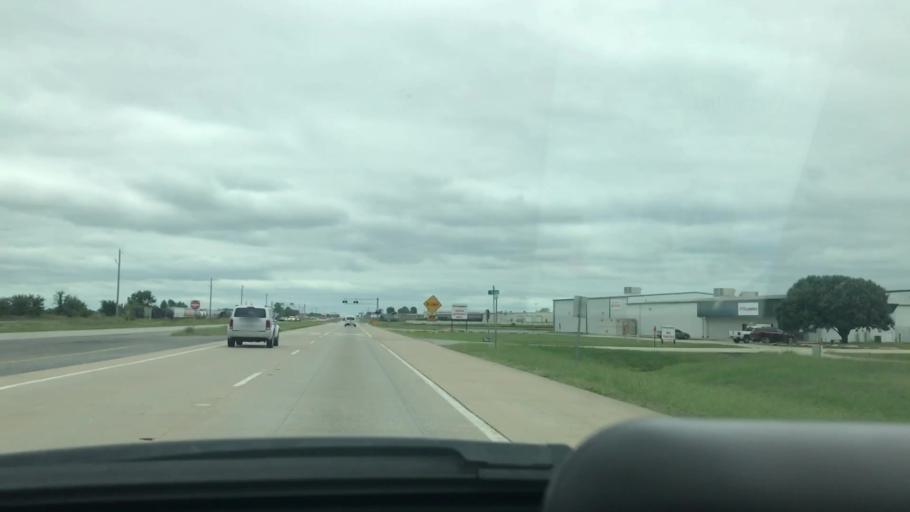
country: US
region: Oklahoma
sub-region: Mayes County
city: Chouteau
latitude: 36.2348
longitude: -95.3387
